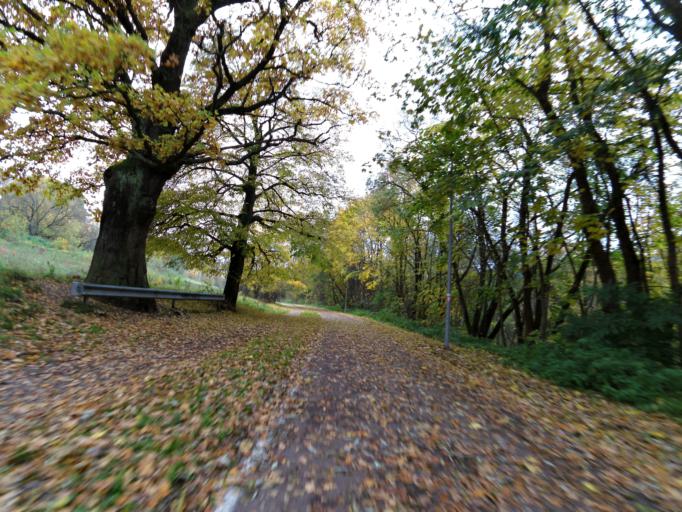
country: LT
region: Vilnius County
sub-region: Vilnius
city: Vilnius
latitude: 54.7276
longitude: 25.3086
